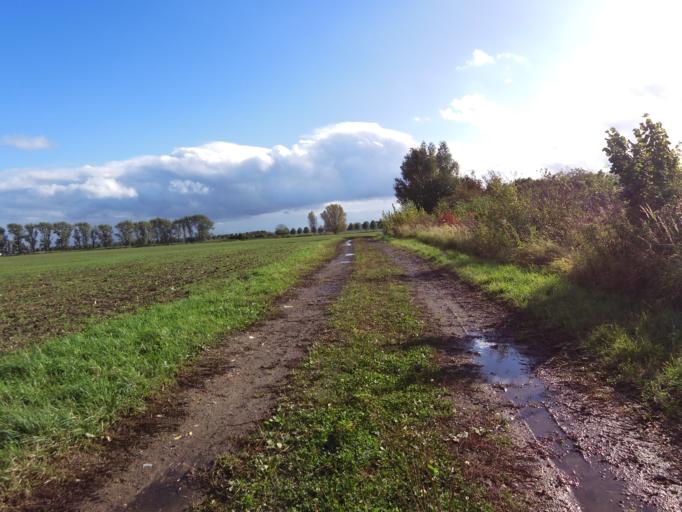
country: DE
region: Saxony
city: Borsdorf
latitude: 51.3231
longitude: 12.4962
